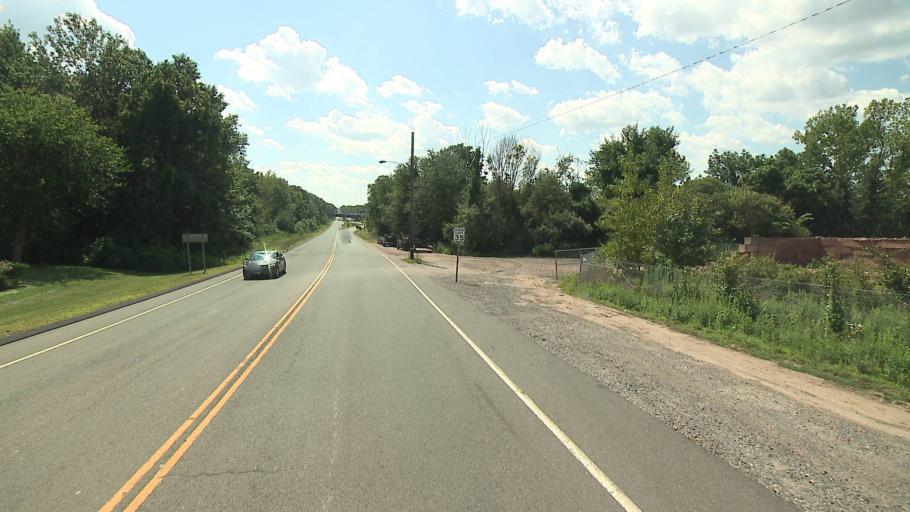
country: US
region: Connecticut
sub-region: Hartford County
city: Farmington
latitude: 41.7220
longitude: -72.7896
